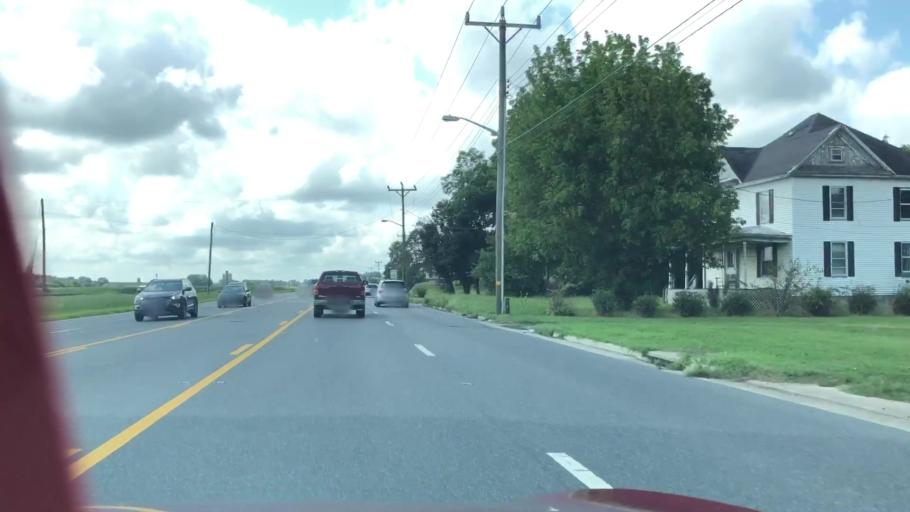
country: US
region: Virginia
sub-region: Northampton County
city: Exmore
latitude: 37.5830
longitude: -75.7869
